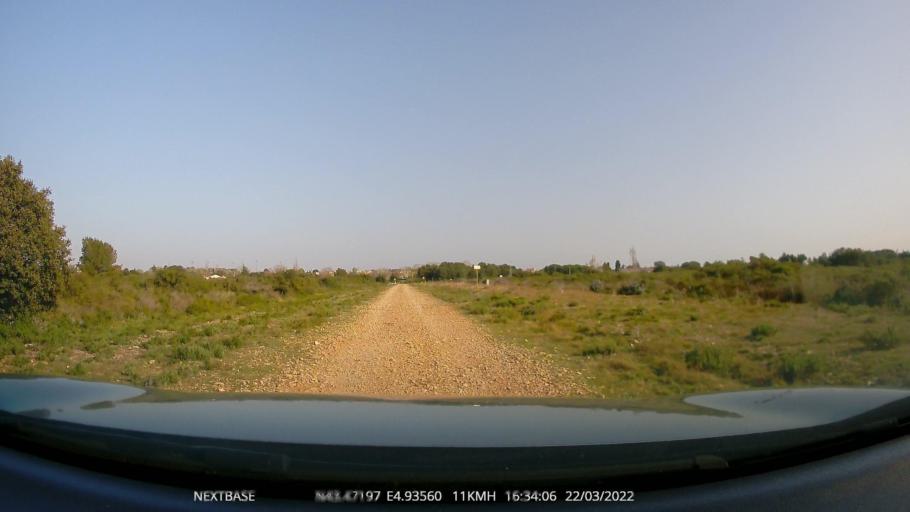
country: FR
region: Provence-Alpes-Cote d'Azur
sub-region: Departement des Bouches-du-Rhone
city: Fos-sur-Mer
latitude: 43.4720
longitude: 4.9357
